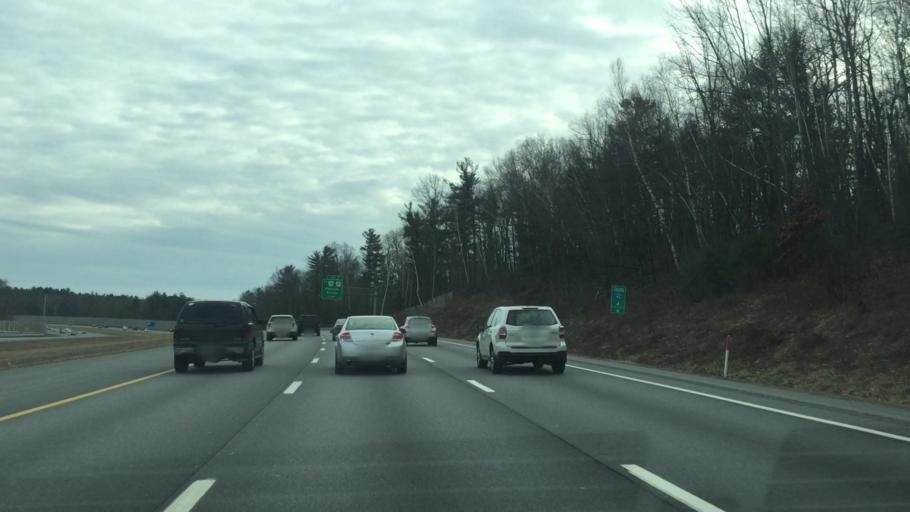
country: US
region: New Hampshire
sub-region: Rockingham County
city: Windham
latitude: 42.7886
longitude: -71.2691
